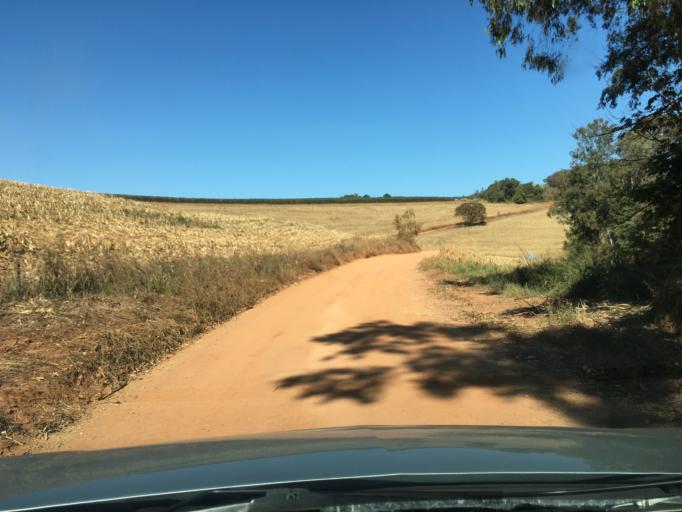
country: BR
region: Minas Gerais
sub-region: Campestre
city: Campestre
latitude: -21.5817
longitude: -46.2032
